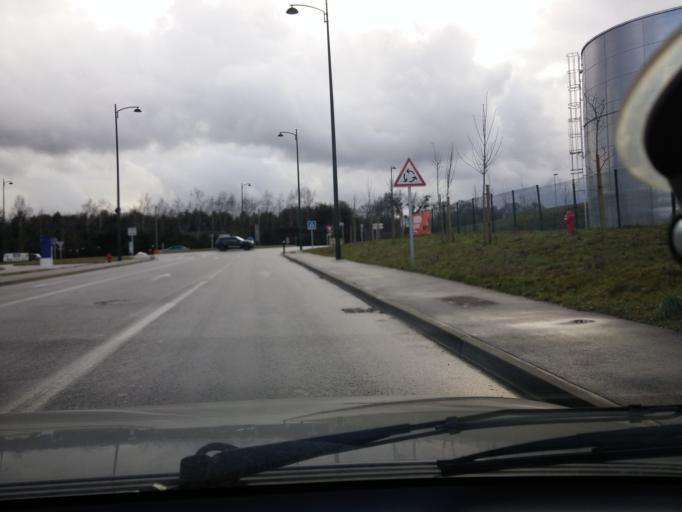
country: FR
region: Ile-de-France
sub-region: Departement du Val-de-Marne
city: La Queue-en-Brie
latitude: 48.7758
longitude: 2.5929
